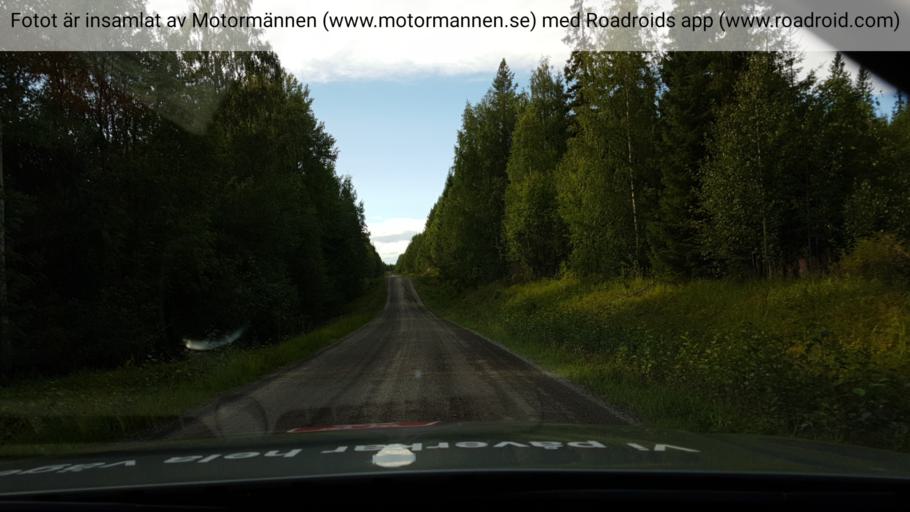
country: SE
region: Jaemtland
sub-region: Braecke Kommun
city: Braecke
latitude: 63.2140
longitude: 15.3678
